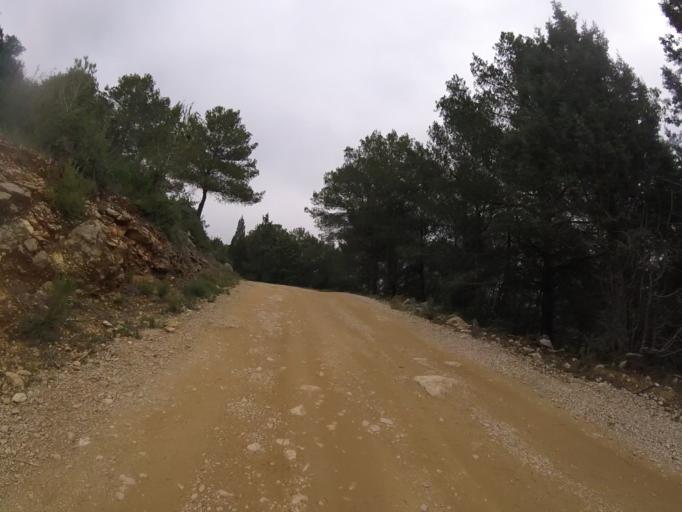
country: ES
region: Valencia
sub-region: Provincia de Castello
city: Alcala de Xivert
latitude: 40.3039
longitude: 0.2560
